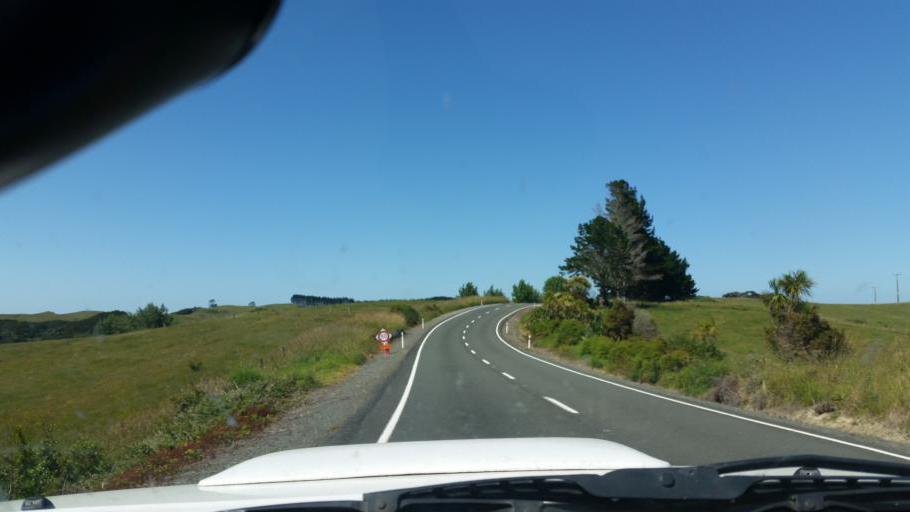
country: NZ
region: Auckland
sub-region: Auckland
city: Wellsford
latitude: -36.2221
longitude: 174.3794
